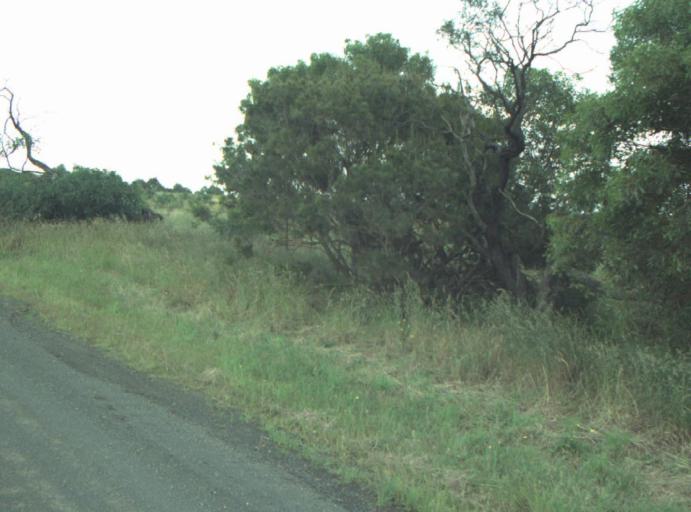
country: AU
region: Victoria
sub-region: Greater Geelong
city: Clifton Springs
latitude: -38.1891
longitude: 144.5802
